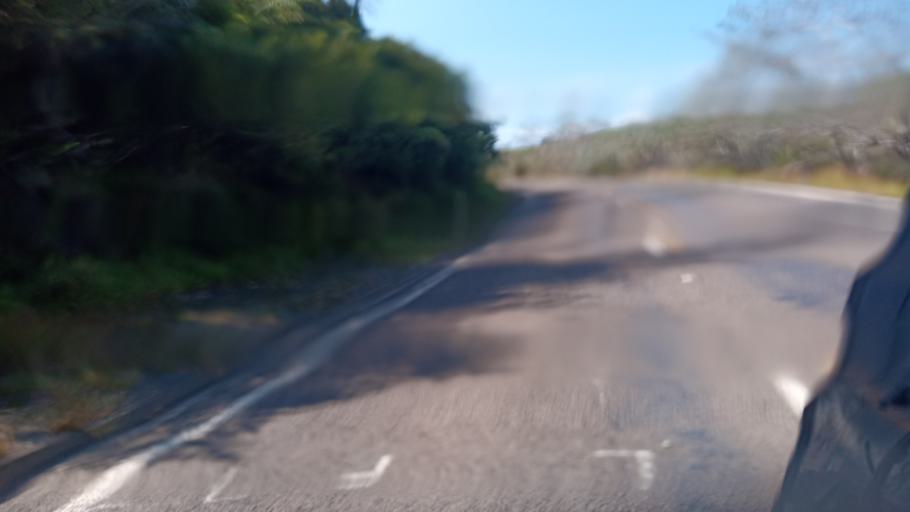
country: NZ
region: Gisborne
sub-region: Gisborne District
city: Gisborne
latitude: -38.4714
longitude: 178.2644
